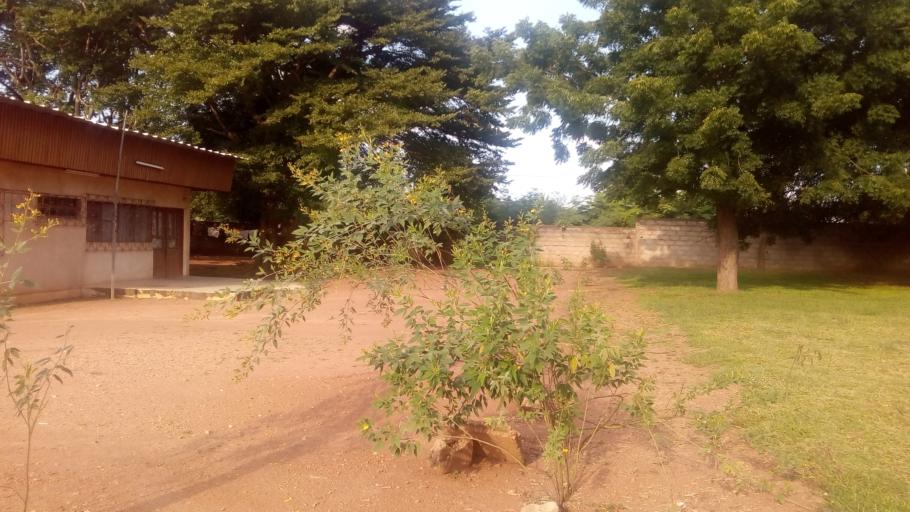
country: CI
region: Vallee du Bandama
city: Bouake
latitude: 7.6863
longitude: -5.0646
